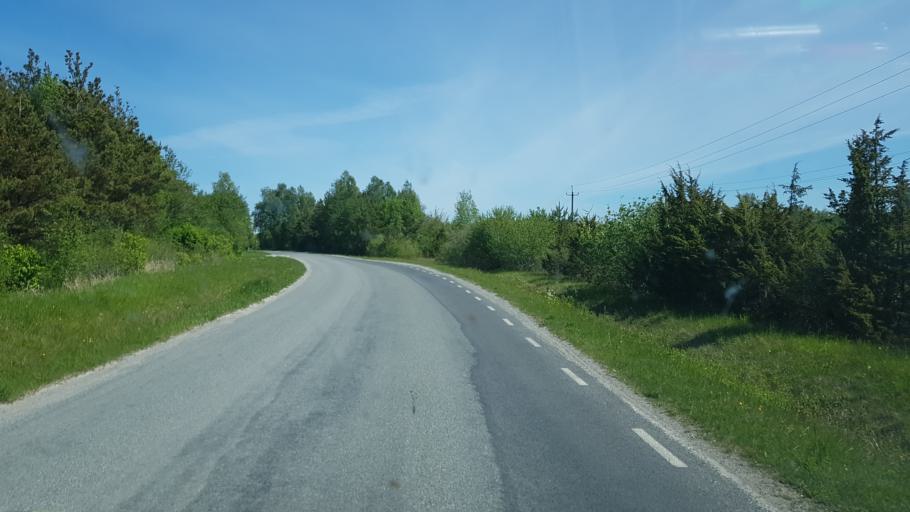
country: EE
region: Saare
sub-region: Kuressaare linn
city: Kuressaare
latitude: 58.2757
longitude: 22.4998
